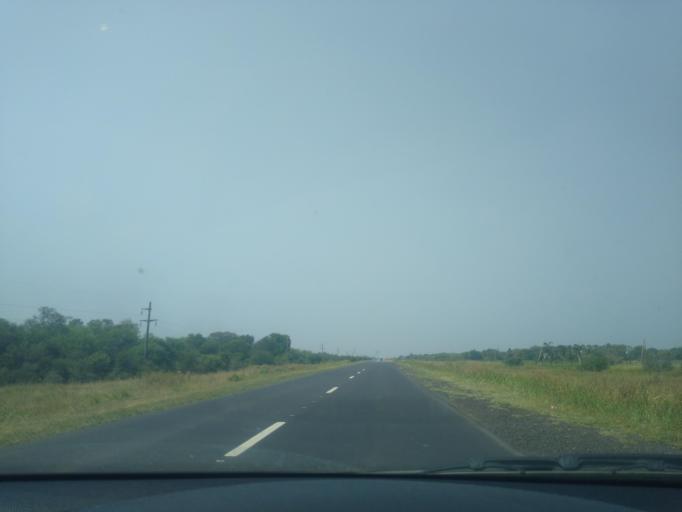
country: AR
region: Chaco
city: Fontana
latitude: -27.5033
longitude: -59.0875
